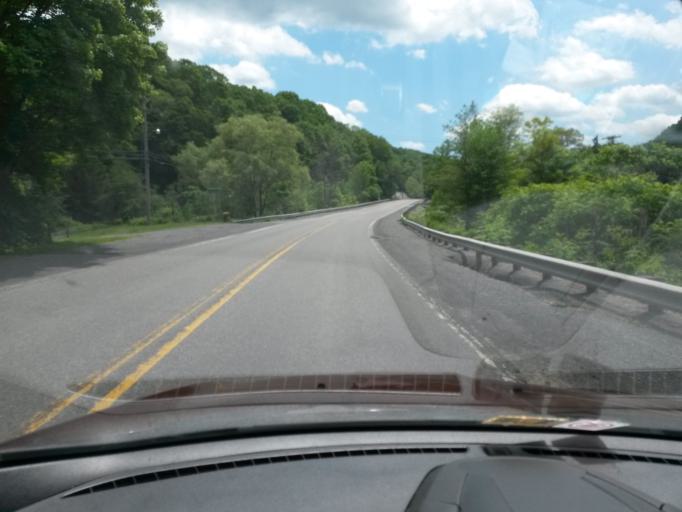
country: US
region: West Virginia
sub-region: Greenbrier County
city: Rainelle
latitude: 38.0489
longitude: -80.7214
